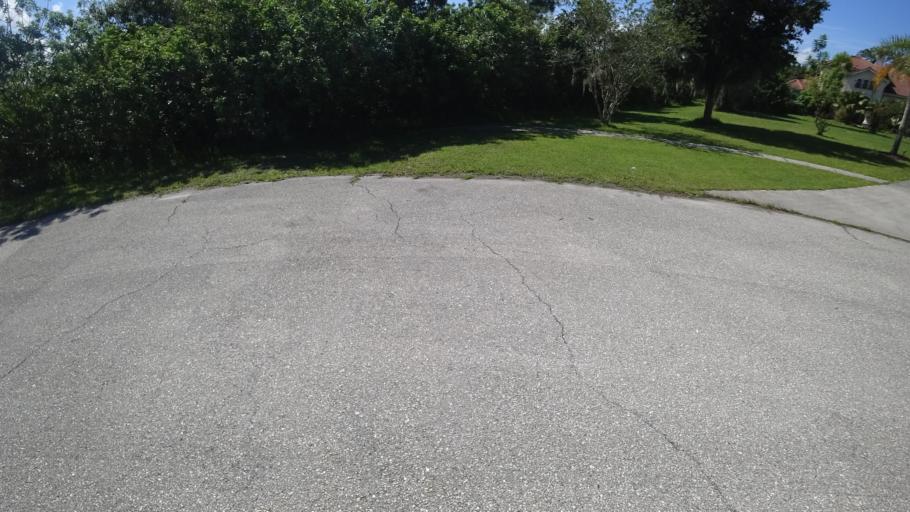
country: US
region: Florida
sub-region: Sarasota County
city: Lake Sarasota
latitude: 27.3895
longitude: -82.3017
